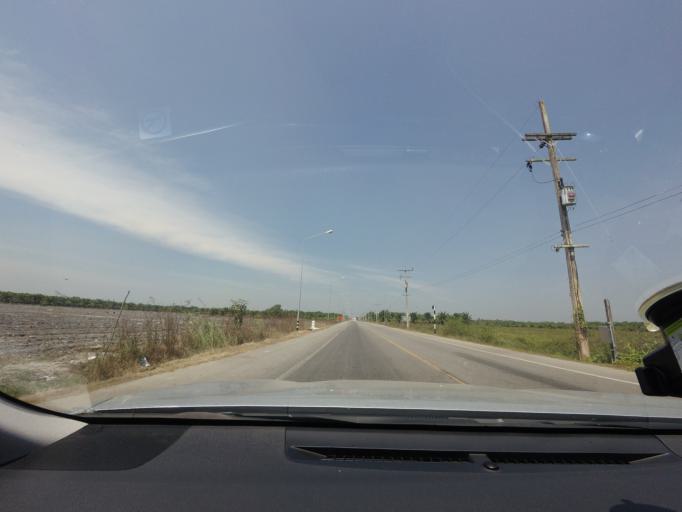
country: TH
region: Surat Thani
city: Tha Chang
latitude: 9.2188
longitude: 99.1802
